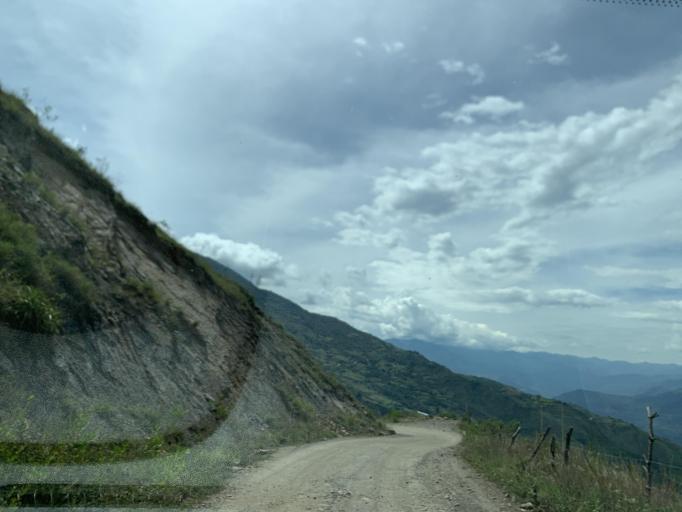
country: CO
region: Boyaca
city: Tipacoque
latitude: 6.4511
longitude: -72.7066
